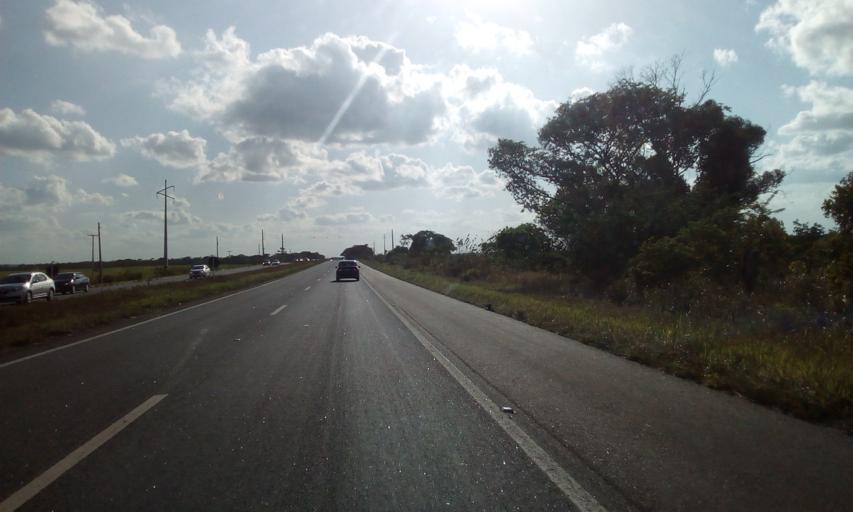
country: BR
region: Paraiba
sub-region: Cruz Do Espirito Santo
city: Cruz do Espirito Santo
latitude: -7.1708
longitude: -35.0353
